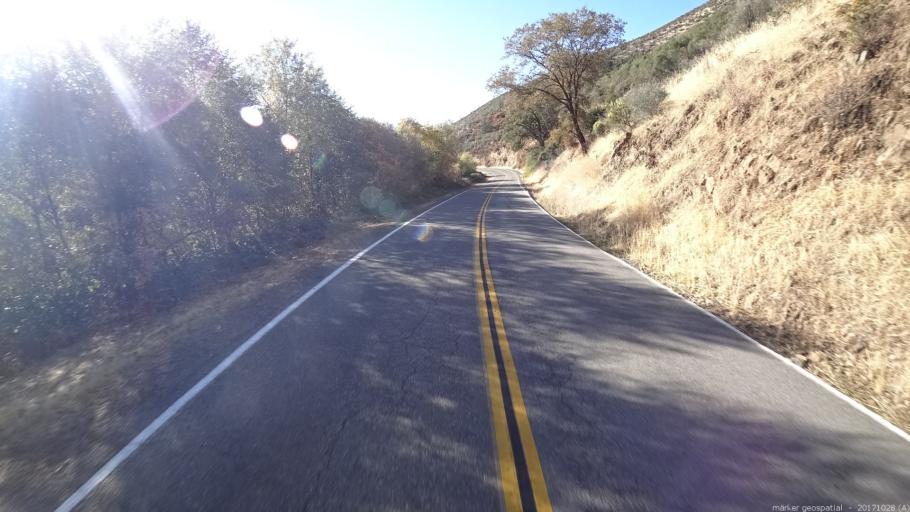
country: US
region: California
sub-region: Trinity County
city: Lewiston
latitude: 40.7151
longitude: -122.6372
